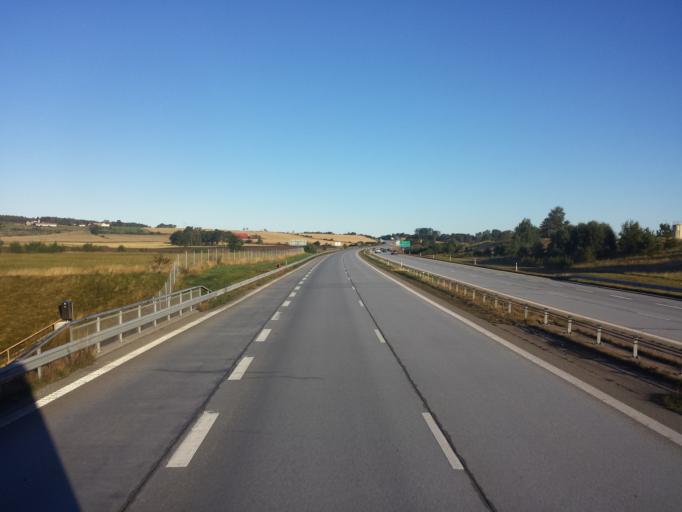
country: SE
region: Halland
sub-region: Falkenbergs Kommun
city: Falkenberg
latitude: 56.8868
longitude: 12.6029
